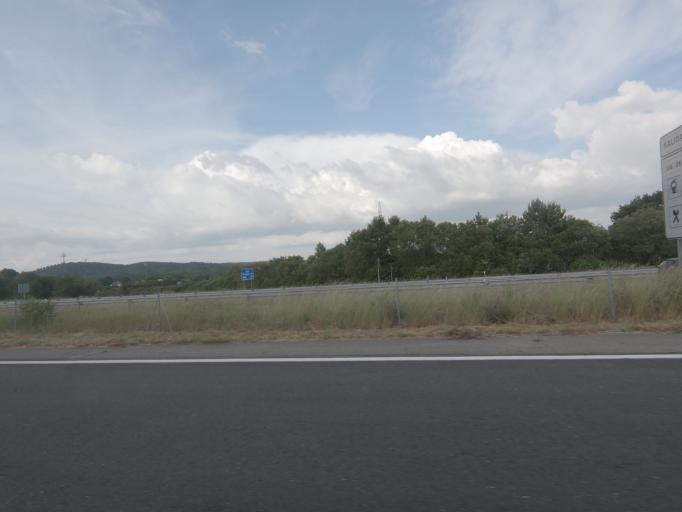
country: ES
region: Galicia
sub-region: Provincia de Ourense
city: Ambia
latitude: 42.1604
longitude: -7.7603
